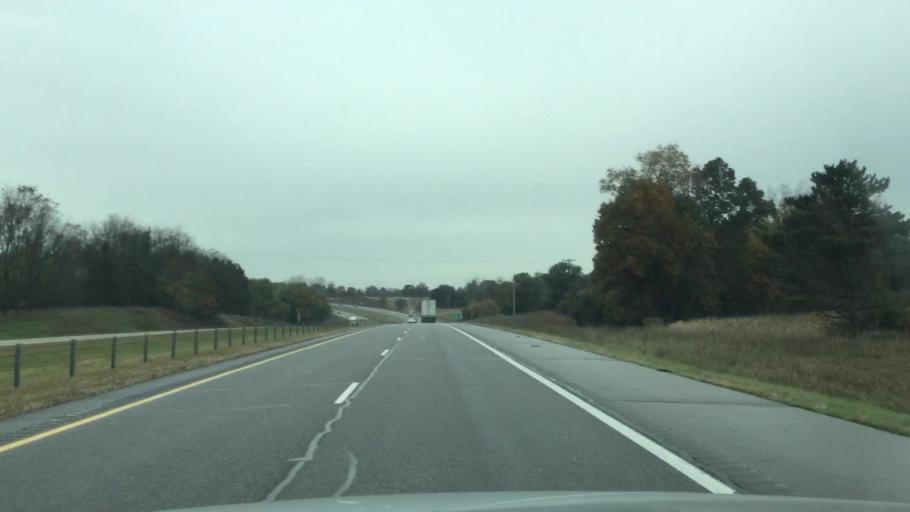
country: US
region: Michigan
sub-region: Calhoun County
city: Albion
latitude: 42.2770
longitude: -84.7854
